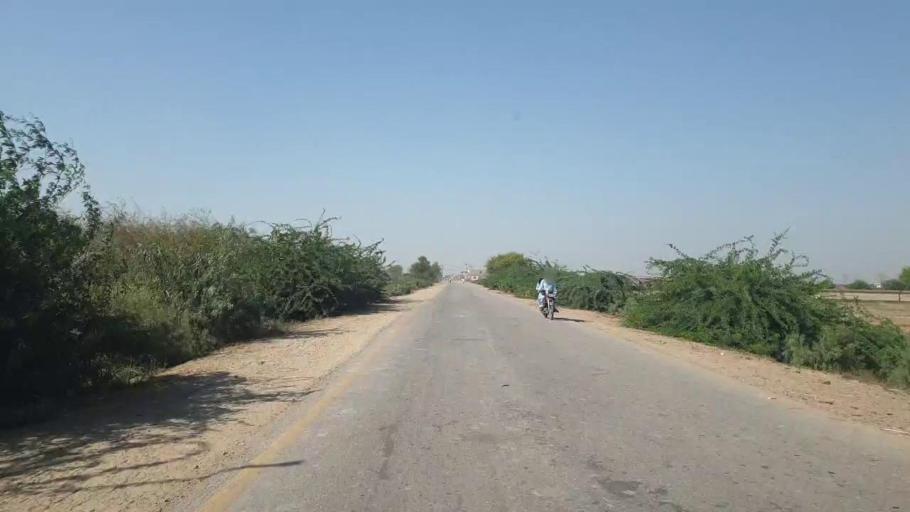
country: PK
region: Sindh
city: Rajo Khanani
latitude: 25.0576
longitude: 68.8027
